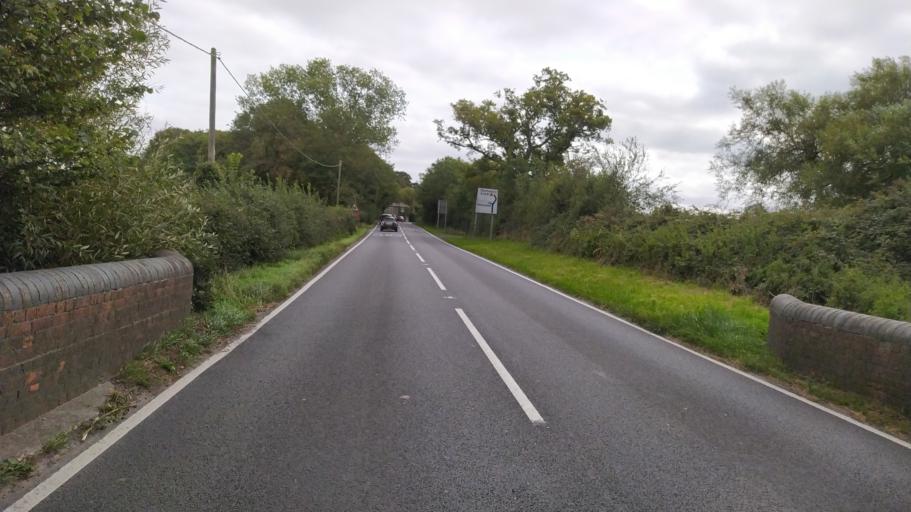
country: GB
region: England
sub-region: Dorset
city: Gillingham
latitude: 51.0190
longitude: -2.2392
